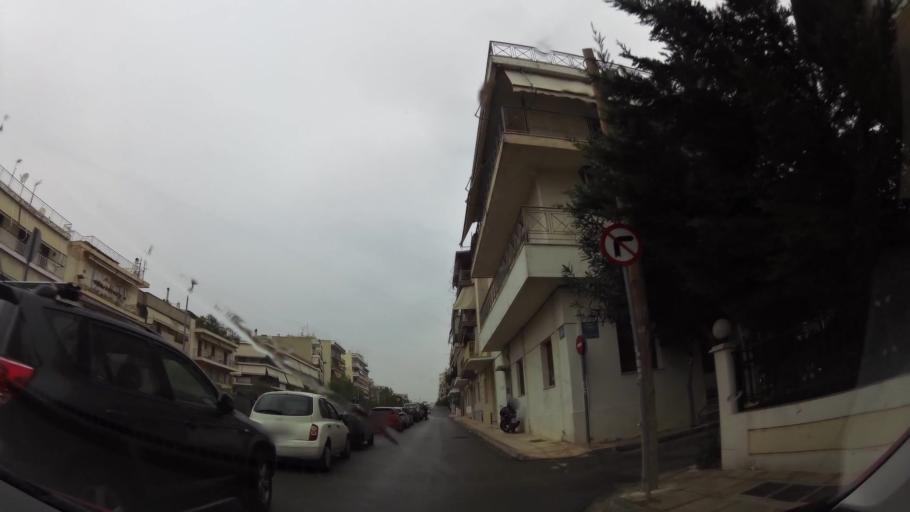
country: GR
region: Attica
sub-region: Nomarchia Athinas
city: Agioi Anargyroi
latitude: 38.0323
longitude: 23.7227
